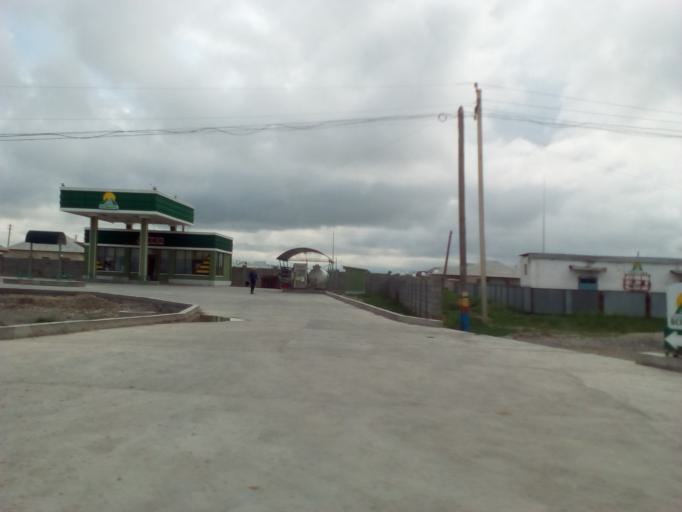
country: KZ
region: Ongtustik Qazaqstan
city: Sholaqqkorghan
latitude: 43.7521
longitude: 69.1945
